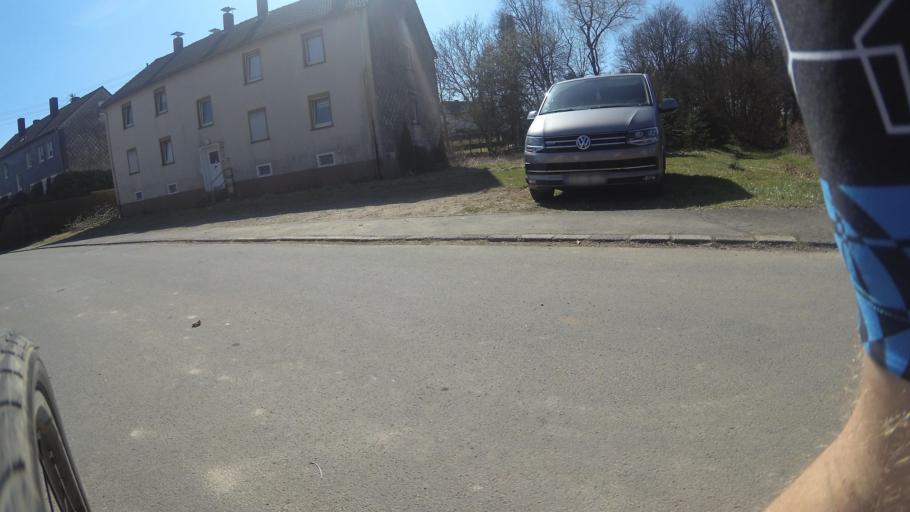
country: DE
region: Rheinland-Pfalz
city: Achtelsbach
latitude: 49.6259
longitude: 7.0816
